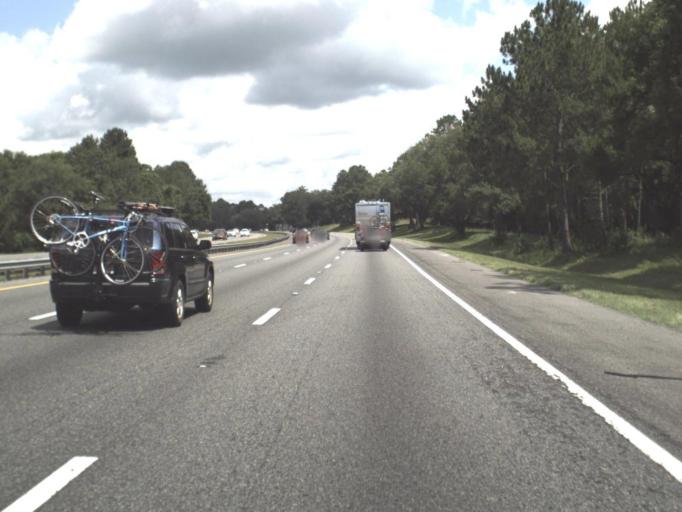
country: US
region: Florida
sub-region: Columbia County
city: Five Points
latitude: 30.2143
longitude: -82.7060
